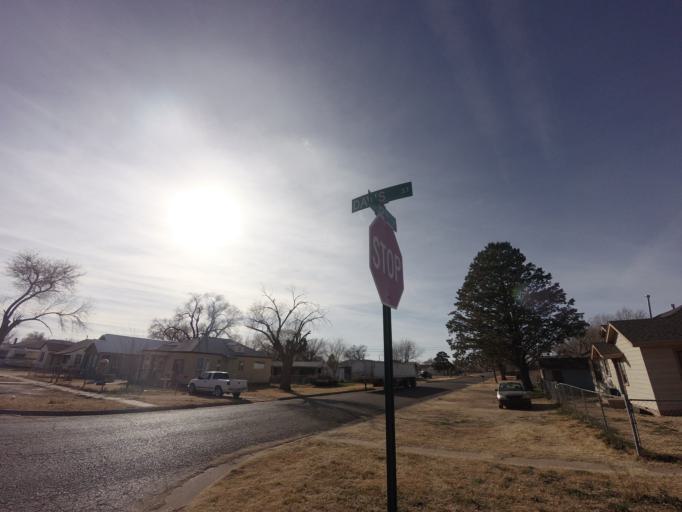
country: US
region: New Mexico
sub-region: Curry County
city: Clovis
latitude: 34.4100
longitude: -103.2168
